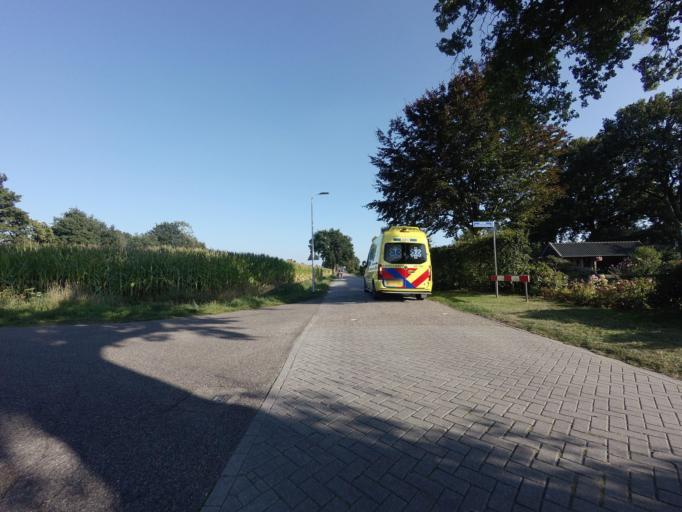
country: NL
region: Overijssel
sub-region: Gemeente Hardenberg
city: Hardenberg
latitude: 52.5617
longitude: 6.6367
